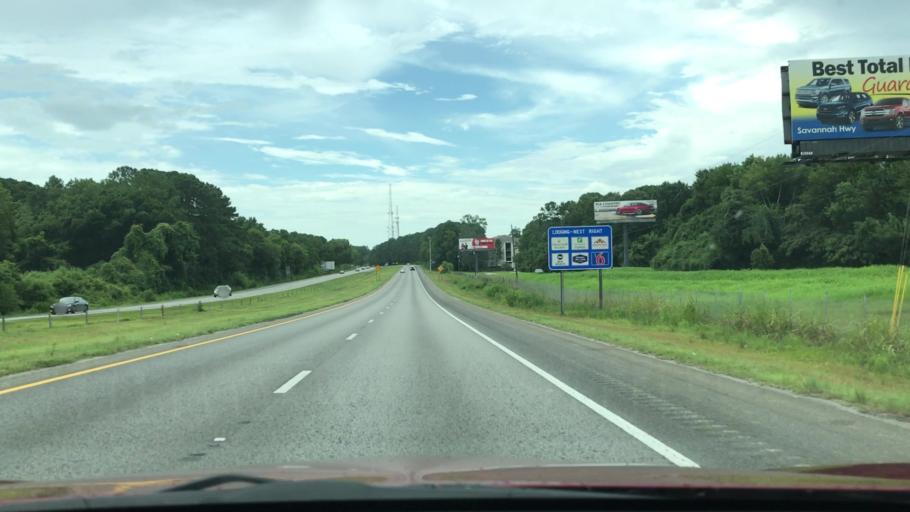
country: US
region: South Carolina
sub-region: Charleston County
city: Shell Point
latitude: 32.8030
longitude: -80.0364
